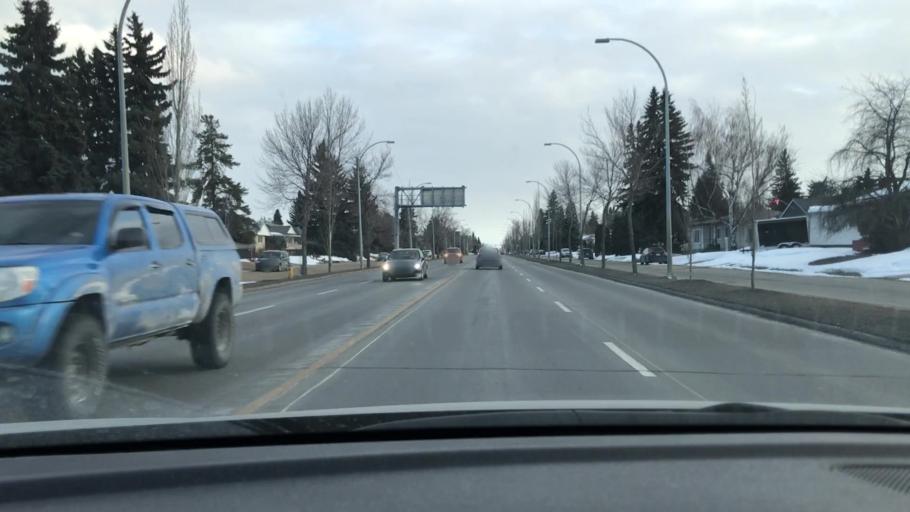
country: CA
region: Alberta
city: Edmonton
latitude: 53.5304
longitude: -113.4429
